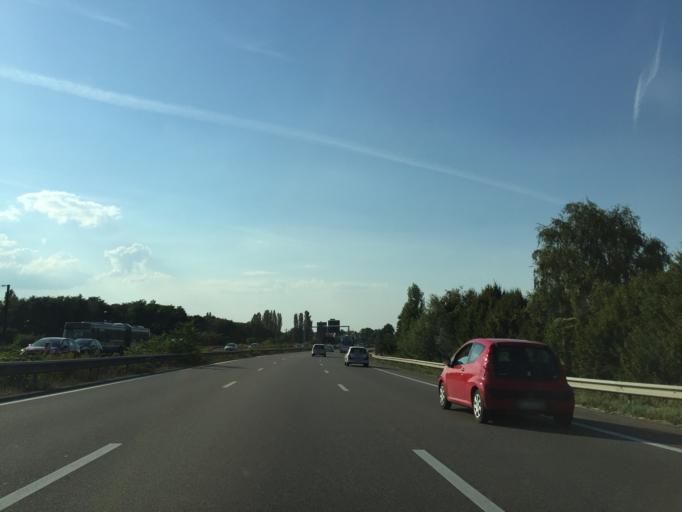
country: FR
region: Alsace
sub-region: Departement du Bas-Rhin
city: Schiltigheim
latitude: 48.6025
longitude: 7.7312
